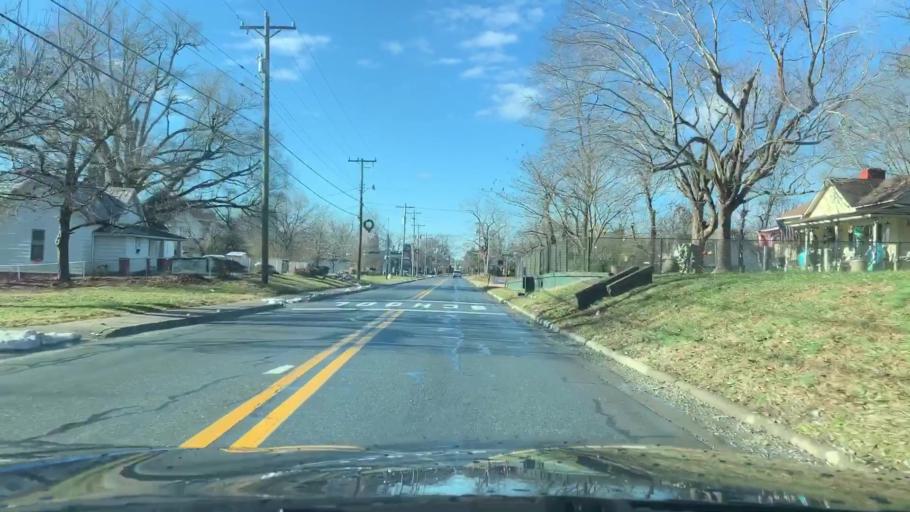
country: US
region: North Carolina
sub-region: Alamance County
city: Haw River
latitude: 36.0936
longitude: -79.3596
